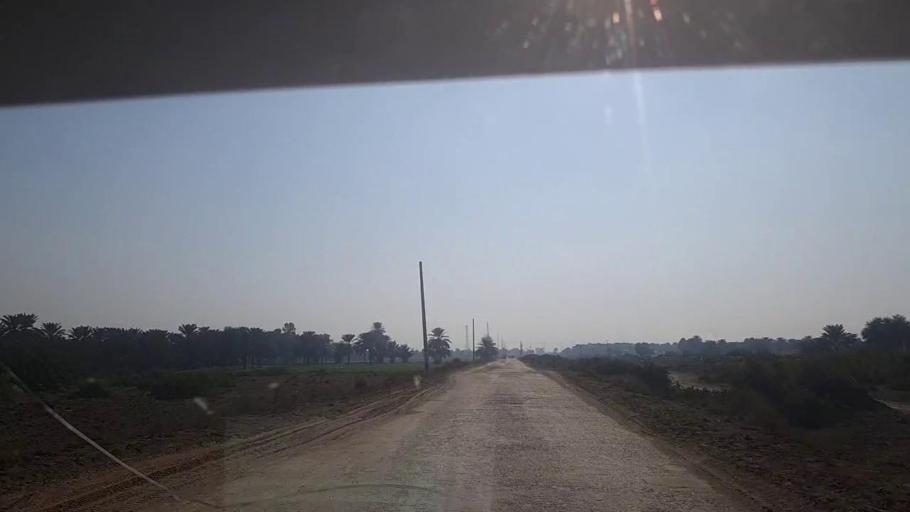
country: PK
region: Sindh
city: Gambat
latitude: 27.3519
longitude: 68.5509
